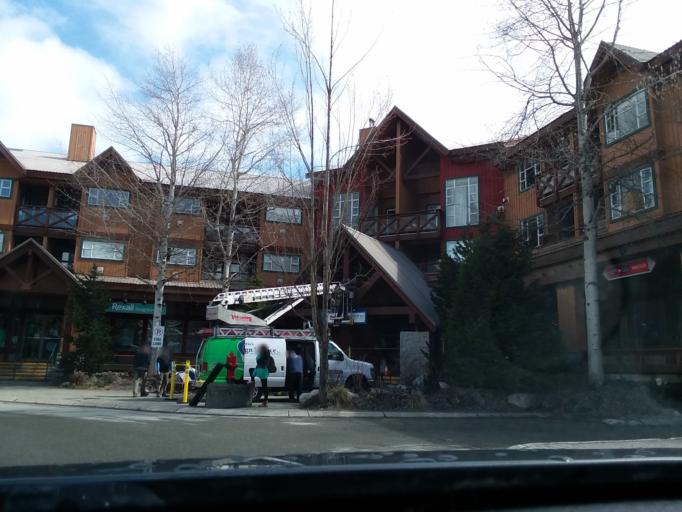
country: CA
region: British Columbia
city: Whistler
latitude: 50.1195
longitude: -122.9562
